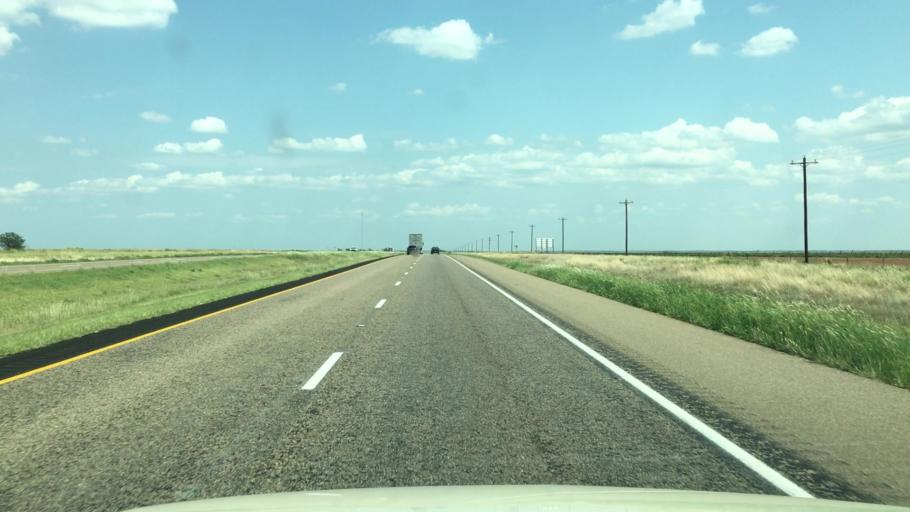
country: US
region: Texas
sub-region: Armstrong County
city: Claude
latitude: 35.0335
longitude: -101.1717
